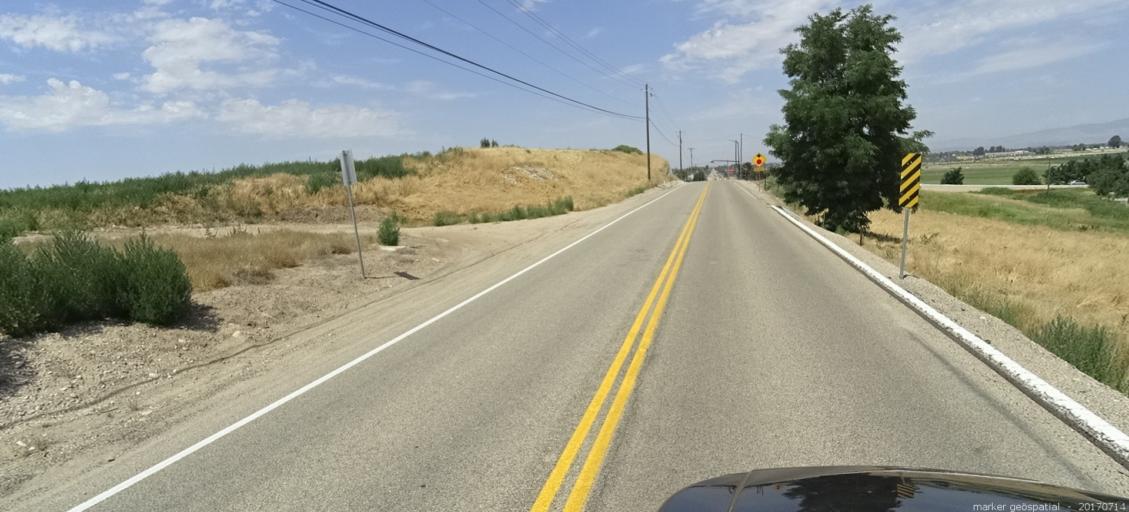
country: US
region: Idaho
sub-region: Ada County
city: Meridian
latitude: 43.5449
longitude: -116.3543
